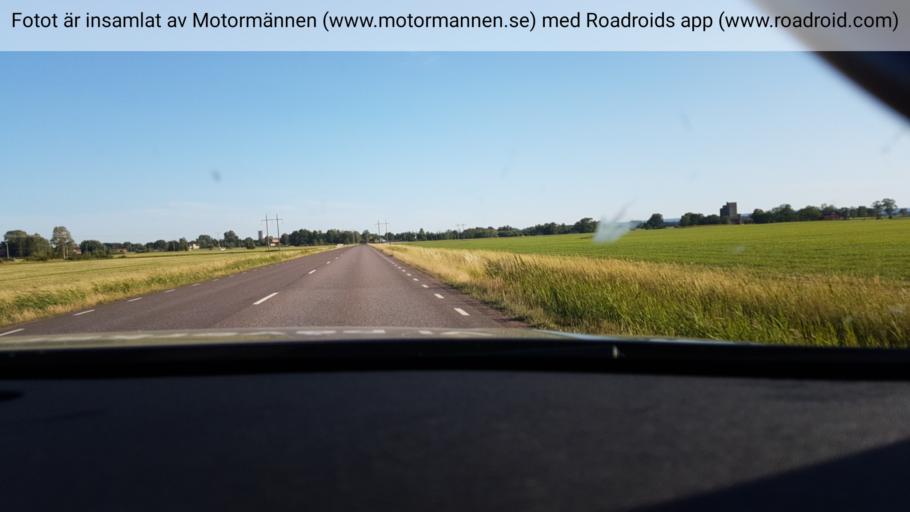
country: SE
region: Vaestra Goetaland
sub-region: Toreboda Kommun
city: Toereboda
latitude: 58.5906
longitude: 14.0078
